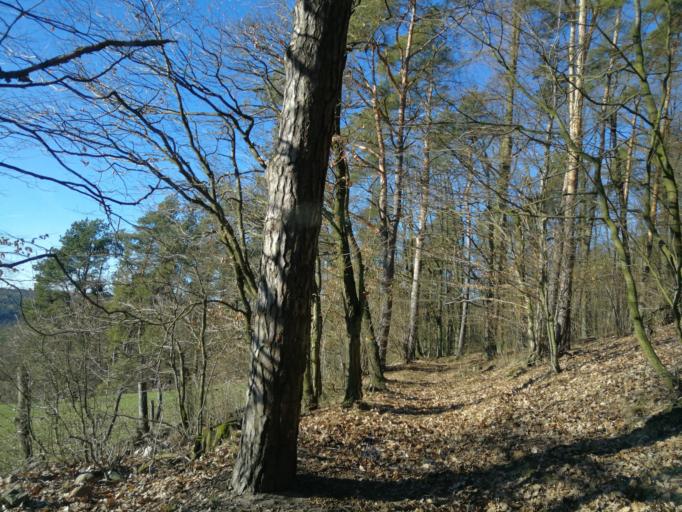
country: PL
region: Kujawsko-Pomorskie
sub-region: Powiat brodnicki
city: Gorzno
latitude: 53.2155
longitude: 19.6699
